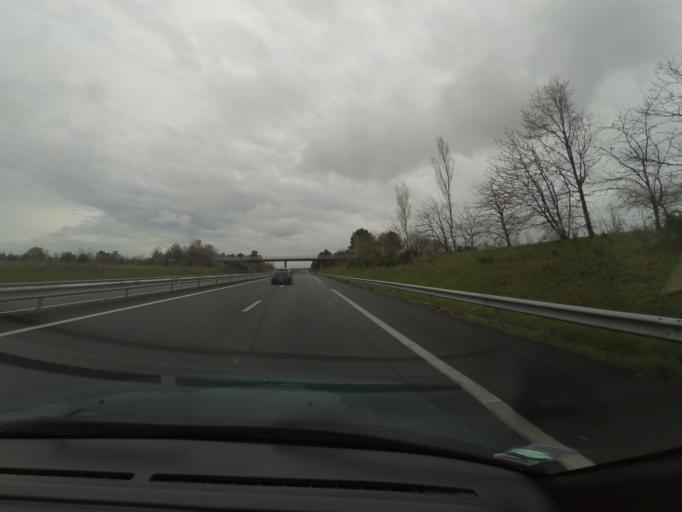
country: FR
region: Pays de la Loire
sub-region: Departement de Maine-et-Loire
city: Durtal
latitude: 47.6364
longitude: -0.2747
